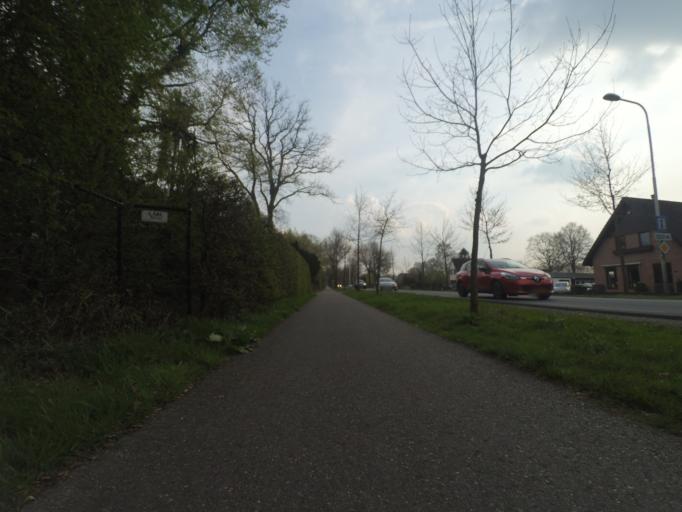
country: NL
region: Gelderland
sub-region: Gemeente Apeldoorn
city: Beekbergen
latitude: 52.1694
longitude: 5.9622
